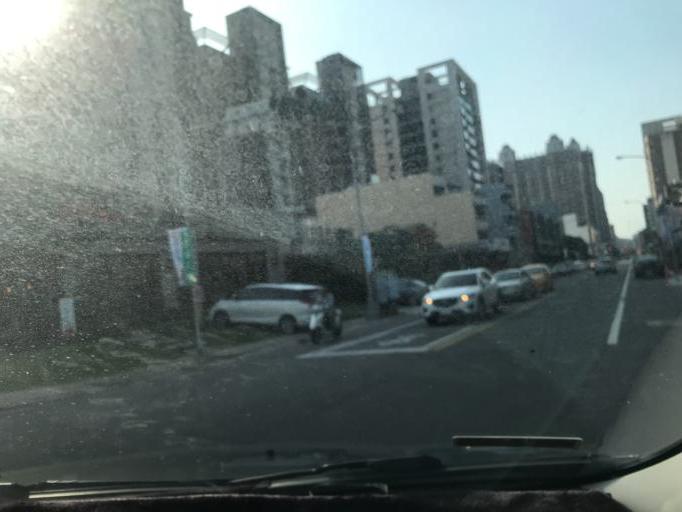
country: TW
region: Taiwan
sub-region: Hsinchu
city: Zhubei
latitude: 24.8153
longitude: 121.0243
